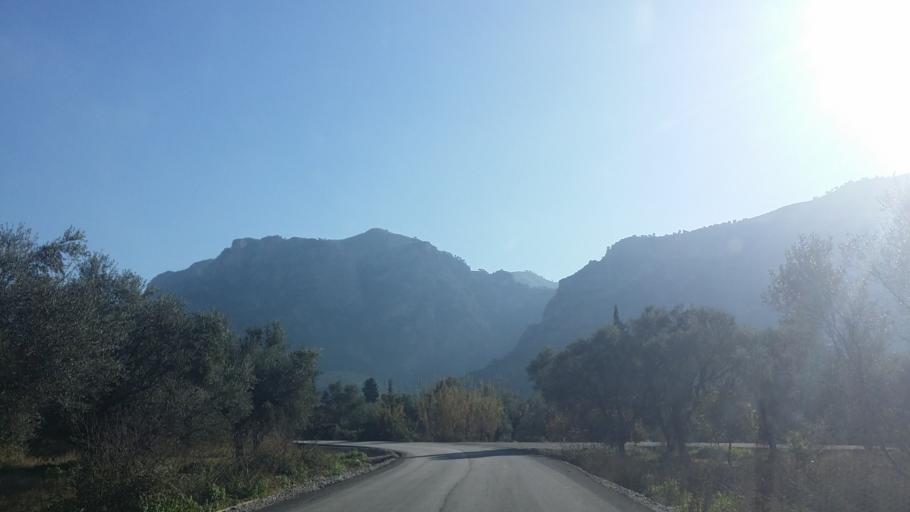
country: GR
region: West Greece
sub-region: Nomos Achaias
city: Temeni
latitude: 38.1935
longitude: 22.1848
